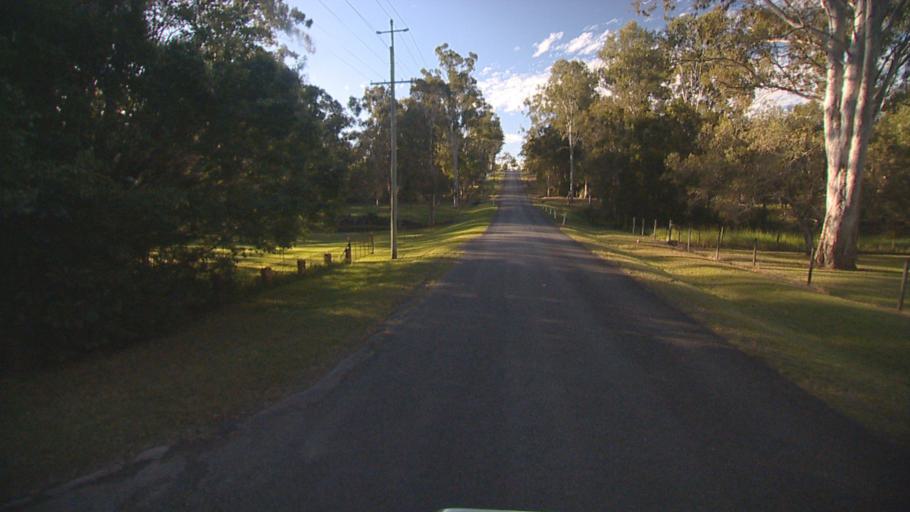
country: AU
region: Queensland
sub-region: Logan
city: Waterford West
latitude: -27.7229
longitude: 153.1536
